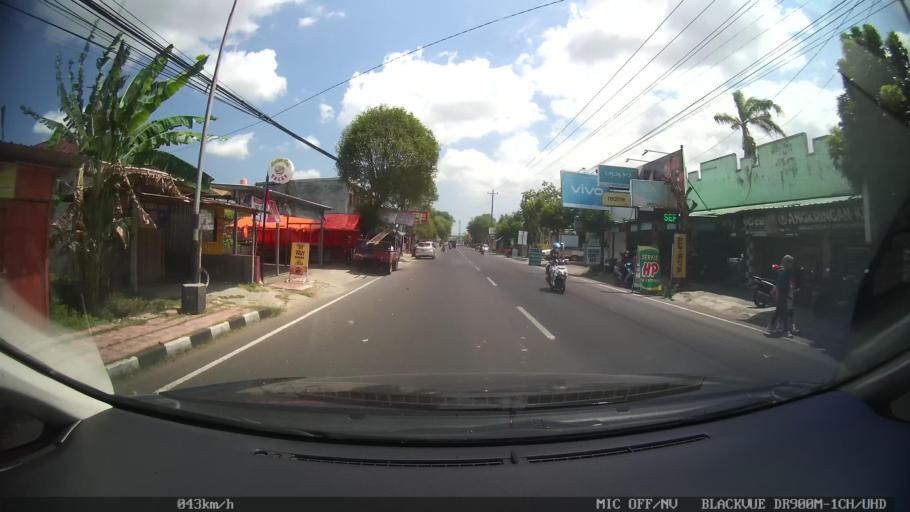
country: ID
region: Daerah Istimewa Yogyakarta
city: Bantul
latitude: -7.8940
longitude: 110.3423
